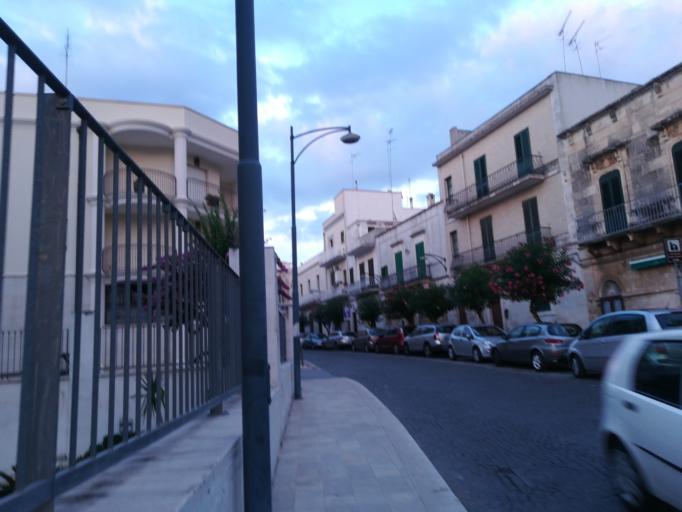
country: IT
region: Apulia
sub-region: Provincia di Brindisi
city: Ostuni
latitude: 40.7314
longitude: 17.5715
